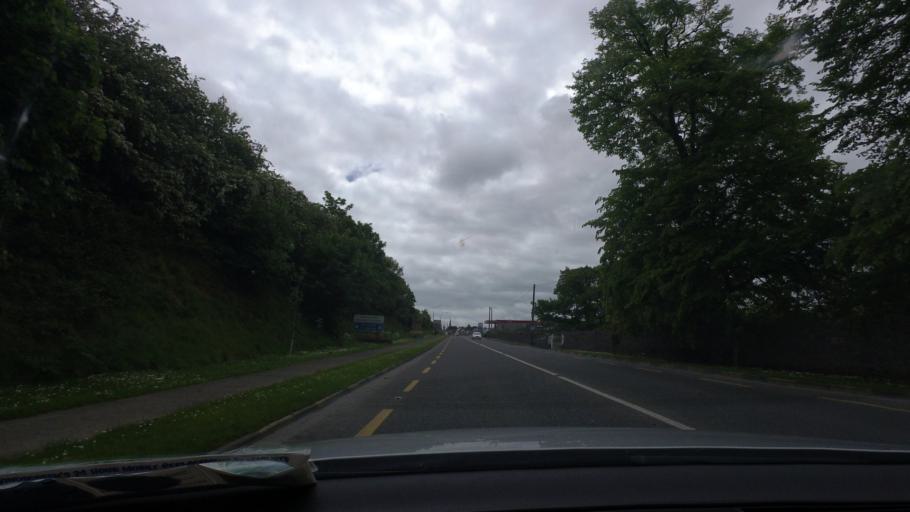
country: IE
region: Munster
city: Cashel
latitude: 52.5223
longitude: -7.8869
